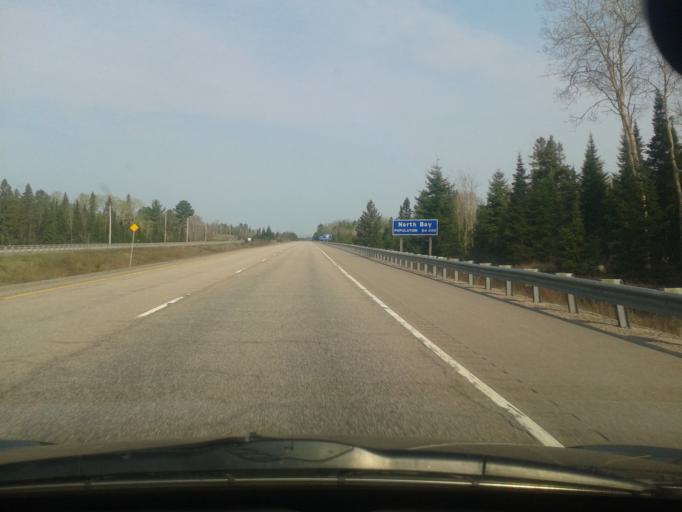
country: CA
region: Ontario
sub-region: Nipissing District
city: North Bay
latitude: 46.2437
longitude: -79.3601
